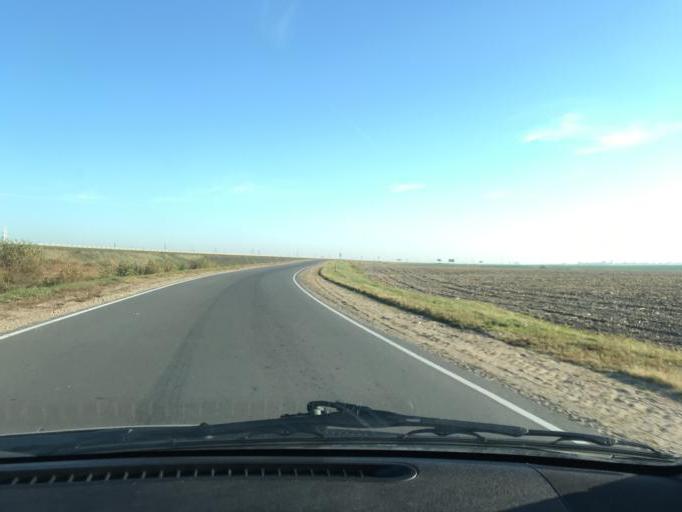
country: BY
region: Brest
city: Asnyezhytsy
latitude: 52.1834
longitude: 26.0829
